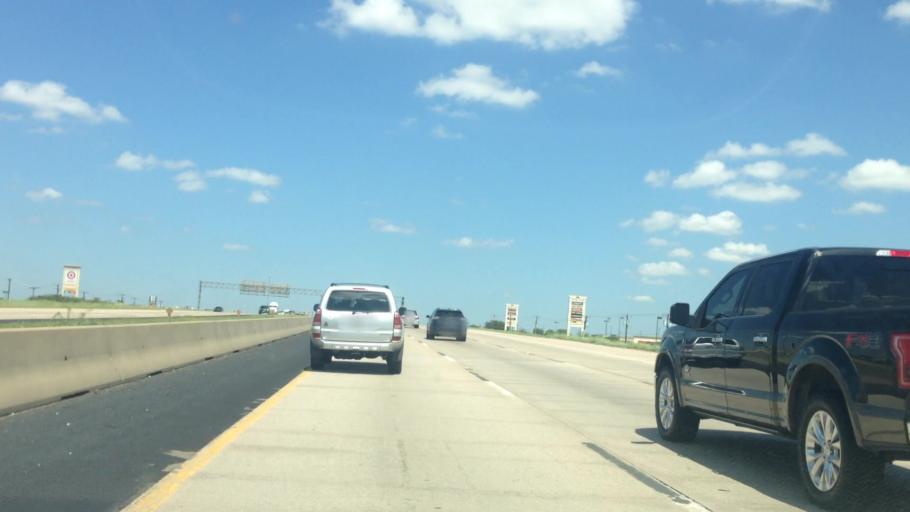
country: US
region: Texas
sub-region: Tarrant County
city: Euless
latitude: 32.8770
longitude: -97.0993
